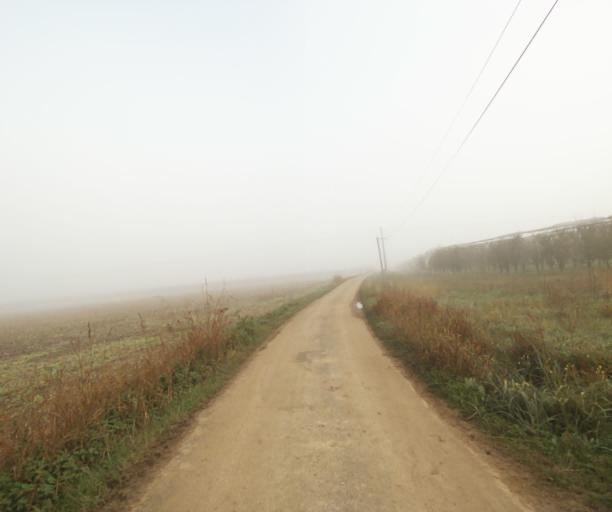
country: FR
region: Midi-Pyrenees
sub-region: Departement du Tarn-et-Garonne
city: Nohic
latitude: 43.9010
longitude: 1.4384
